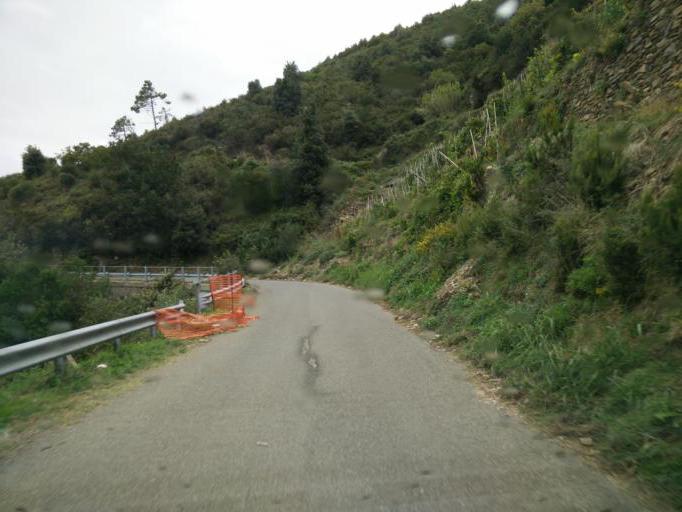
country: IT
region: Liguria
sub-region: Provincia di La Spezia
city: Vernazza
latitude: 44.1425
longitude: 9.6845
